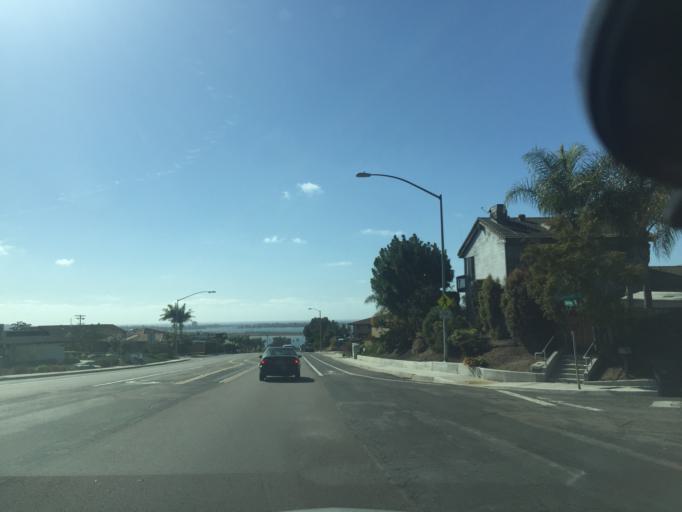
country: US
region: California
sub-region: San Diego County
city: San Diego
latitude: 32.7915
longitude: -117.1978
